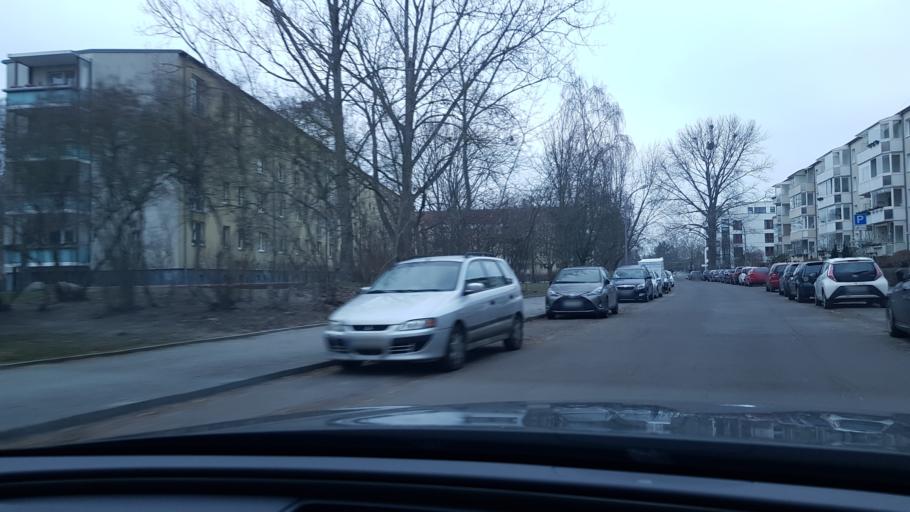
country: DE
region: Berlin
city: Grunau
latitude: 52.4269
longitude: 13.5929
